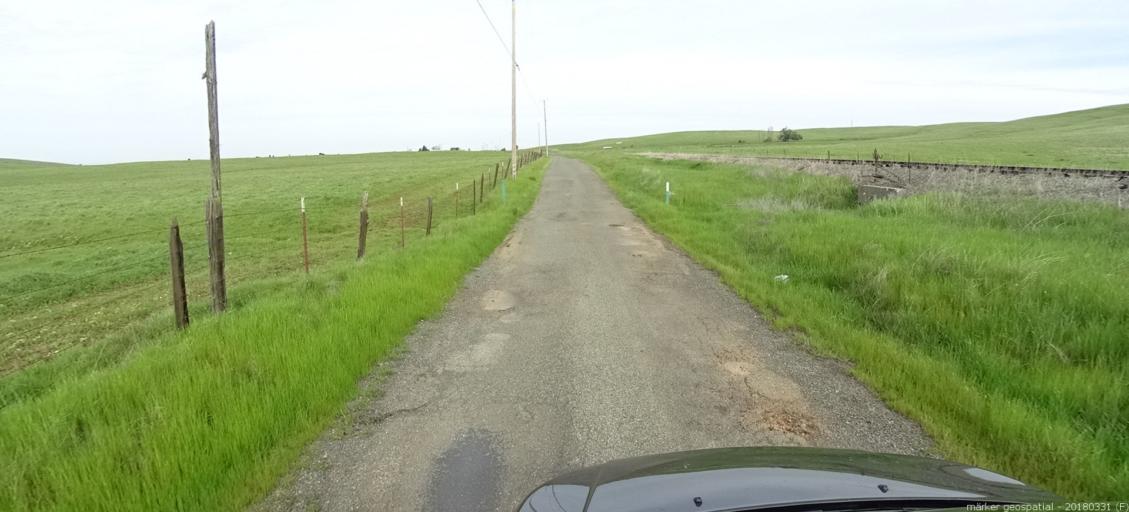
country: US
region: California
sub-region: El Dorado County
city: El Dorado Hills
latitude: 38.6224
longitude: -121.0852
